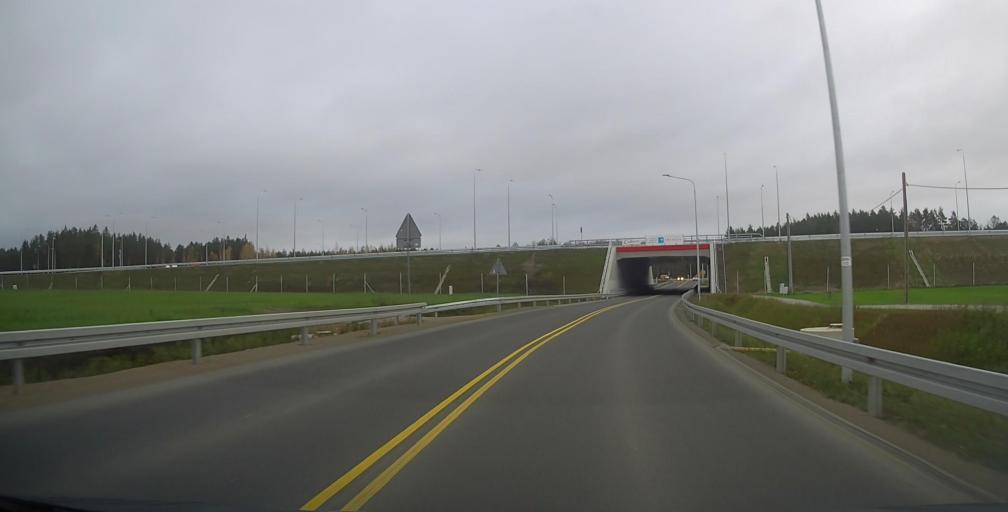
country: PL
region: Warmian-Masurian Voivodeship
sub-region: Powiat elcki
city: Elk
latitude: 53.8381
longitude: 22.4161
